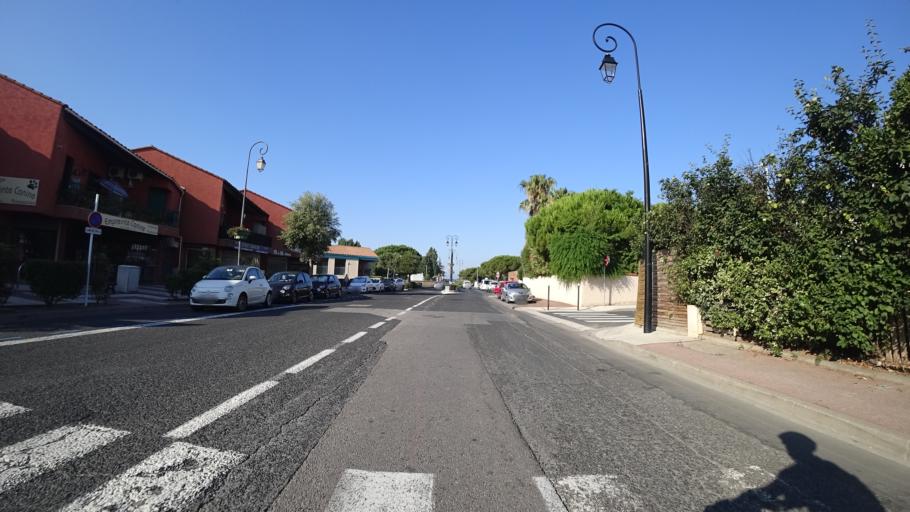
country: FR
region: Languedoc-Roussillon
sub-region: Departement des Pyrenees-Orientales
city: Canet-en-Roussillon
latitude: 42.7044
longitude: 3.0046
